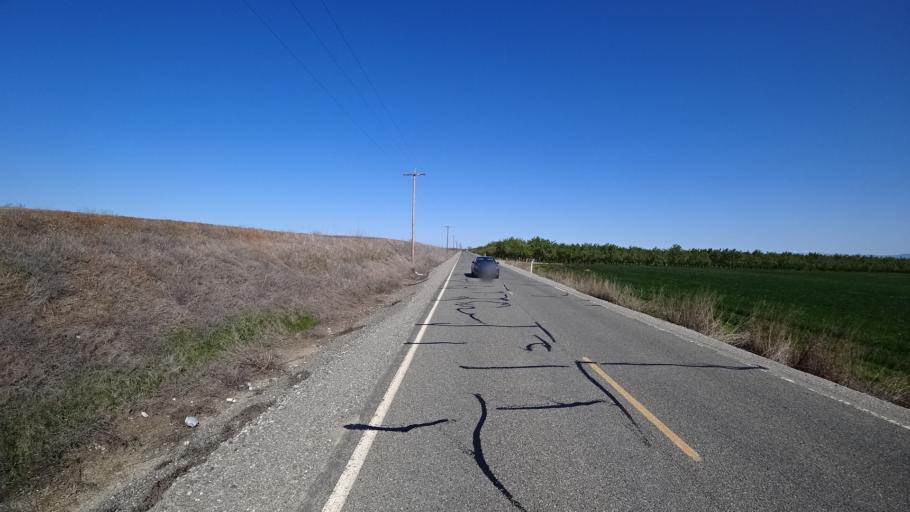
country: US
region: California
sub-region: Glenn County
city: Hamilton City
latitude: 39.7500
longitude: -122.0220
